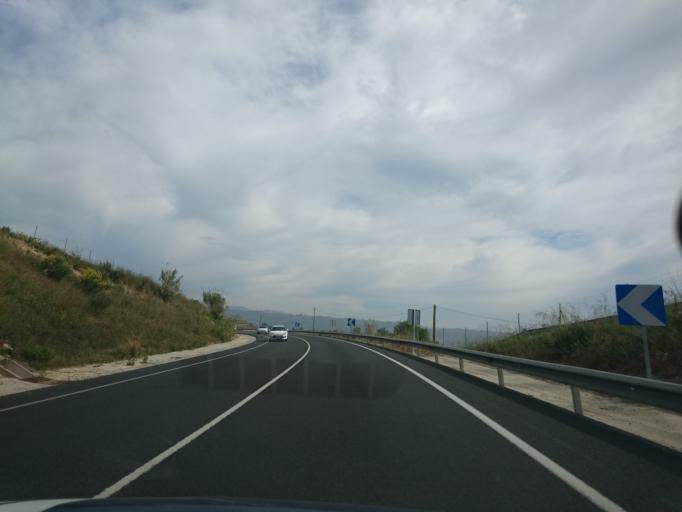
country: ES
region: Catalonia
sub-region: Provincia de Barcelona
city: Sant Pere de Riudebitlles
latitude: 41.4416
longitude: 1.6852
